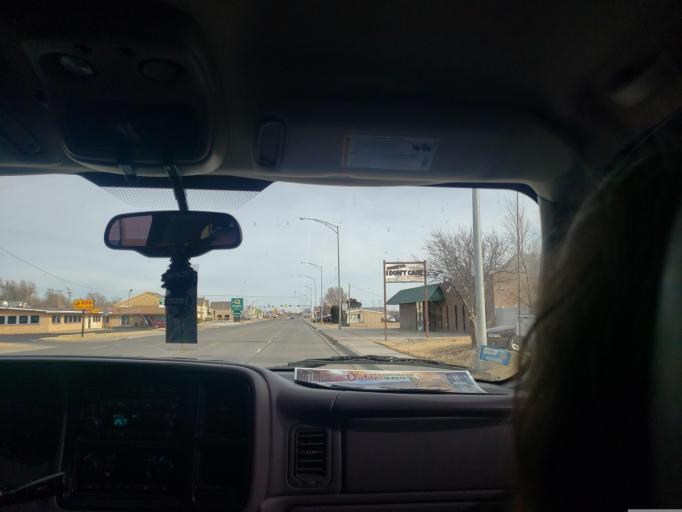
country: US
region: Kansas
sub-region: Ford County
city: Dodge City
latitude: 37.7542
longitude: -100.0435
